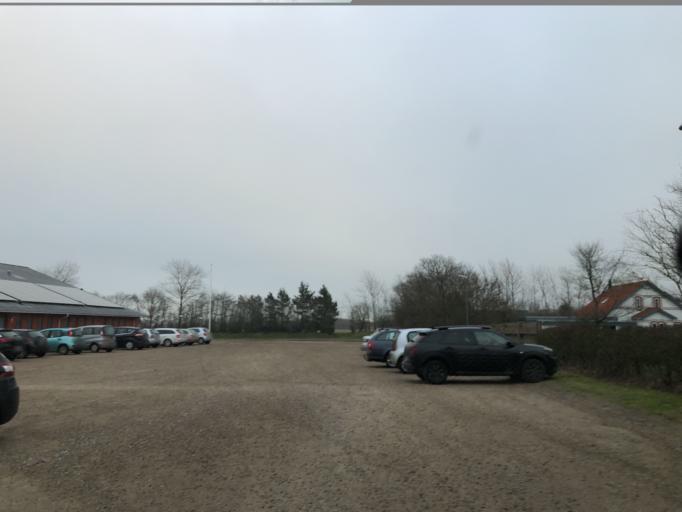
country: DK
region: Central Jutland
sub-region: Holstebro Kommune
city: Ulfborg
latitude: 56.1973
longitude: 8.3112
